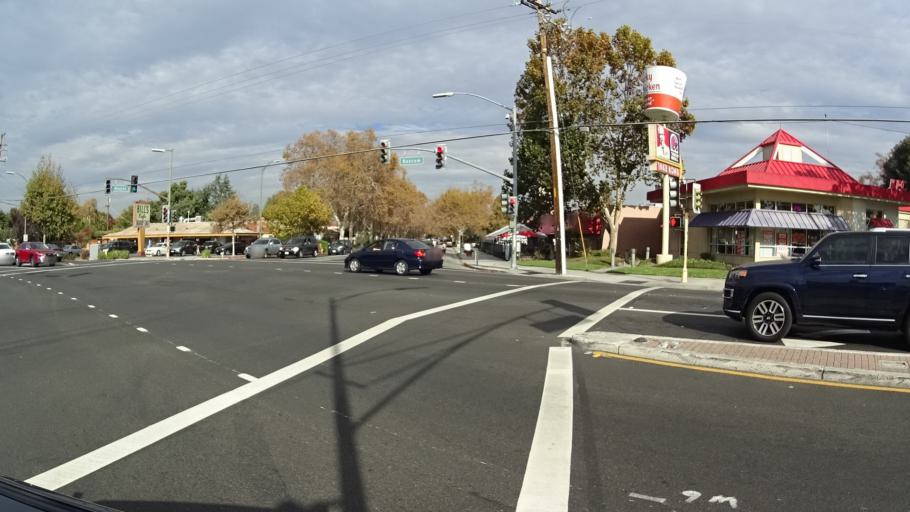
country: US
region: California
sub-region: Santa Clara County
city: Burbank
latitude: 37.3276
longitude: -121.9321
